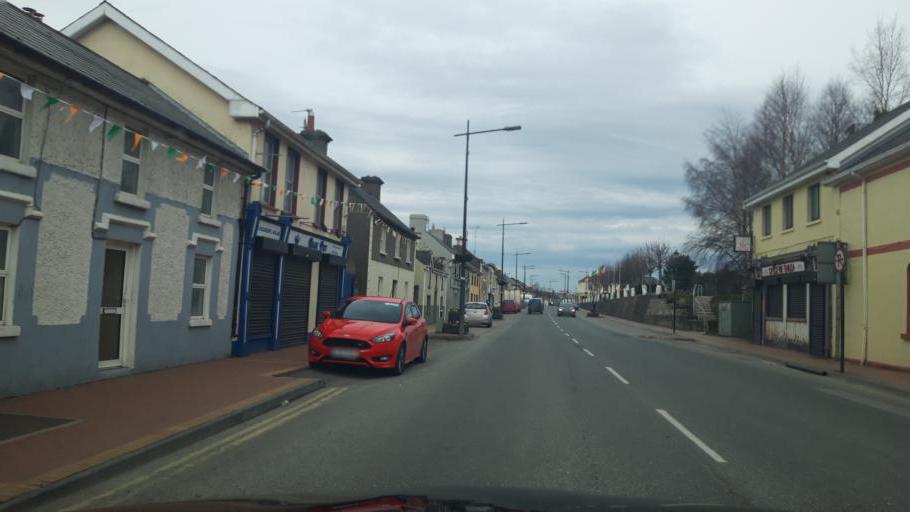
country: IE
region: Leinster
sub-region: Uibh Fhaili
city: Edenderry
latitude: 53.3402
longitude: -7.0570
